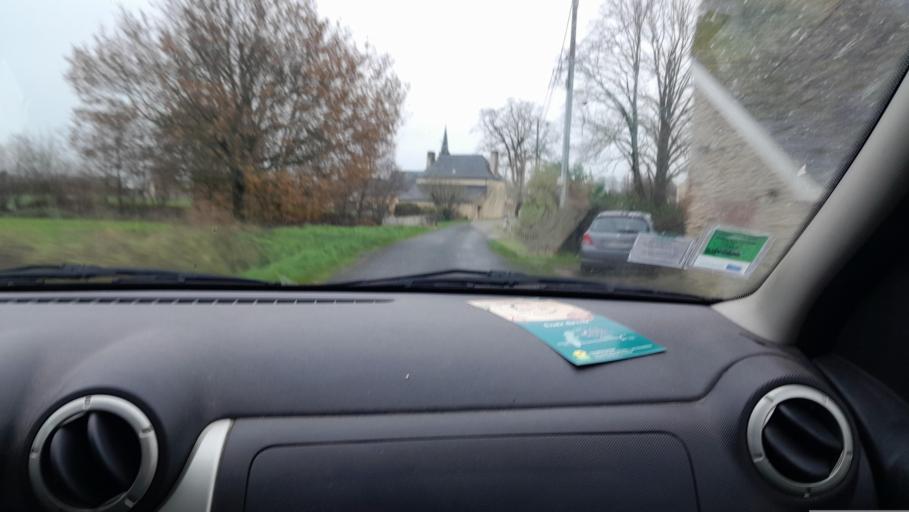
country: FR
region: Brittany
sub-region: Departement d'Ille-et-Vilaine
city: La Guerche-de-Bretagne
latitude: 47.9106
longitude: -1.1442
